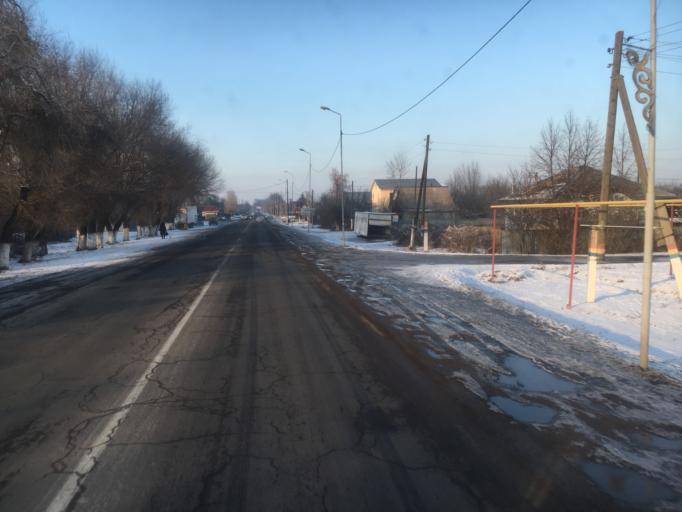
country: KZ
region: Almaty Oblysy
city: Burunday
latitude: 43.3679
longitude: 76.6413
